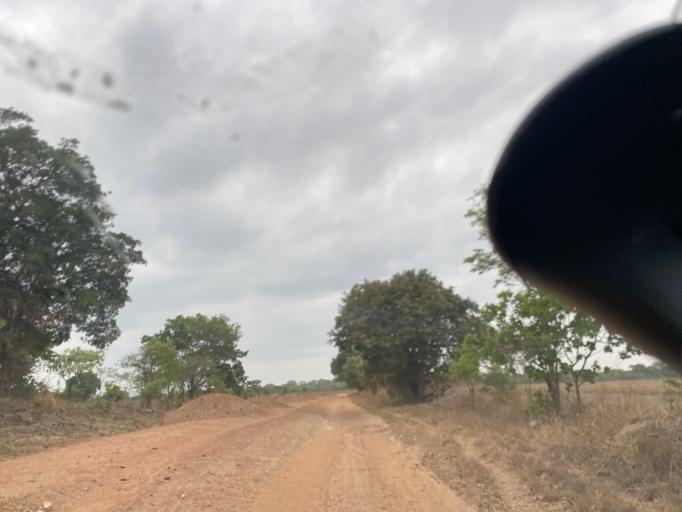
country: ZM
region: Lusaka
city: Chongwe
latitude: -15.2274
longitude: 28.7293
